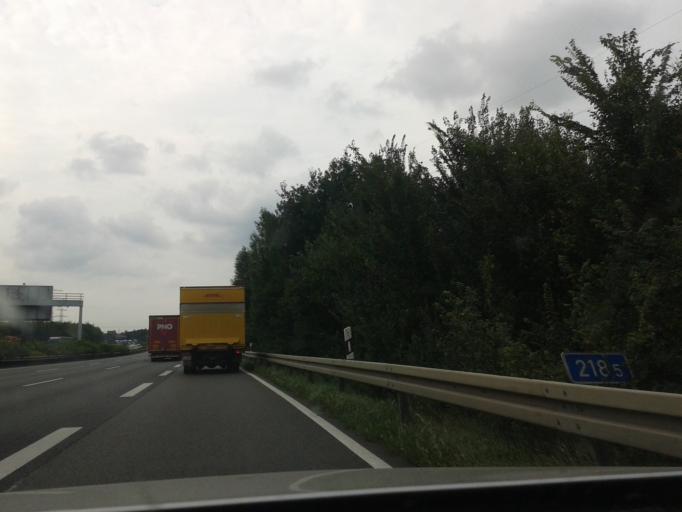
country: DE
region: Lower Saxony
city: Isernhagen Farster Bauerschaft
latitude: 52.4224
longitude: 9.8319
